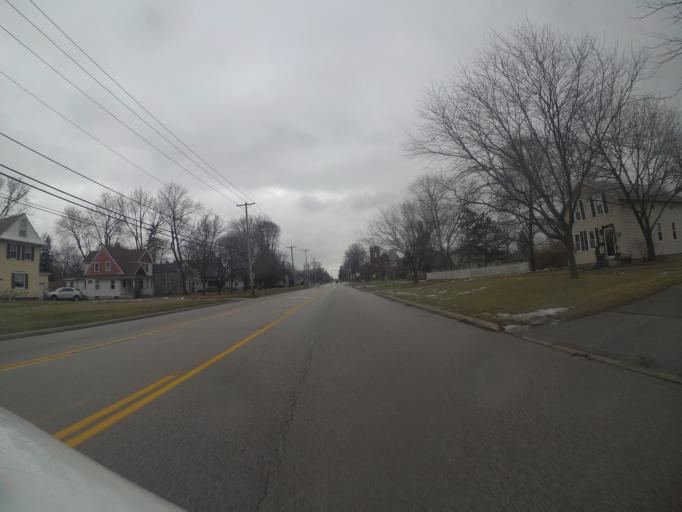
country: US
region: Ohio
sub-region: Wood County
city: Perrysburg
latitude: 41.5581
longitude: -83.6250
